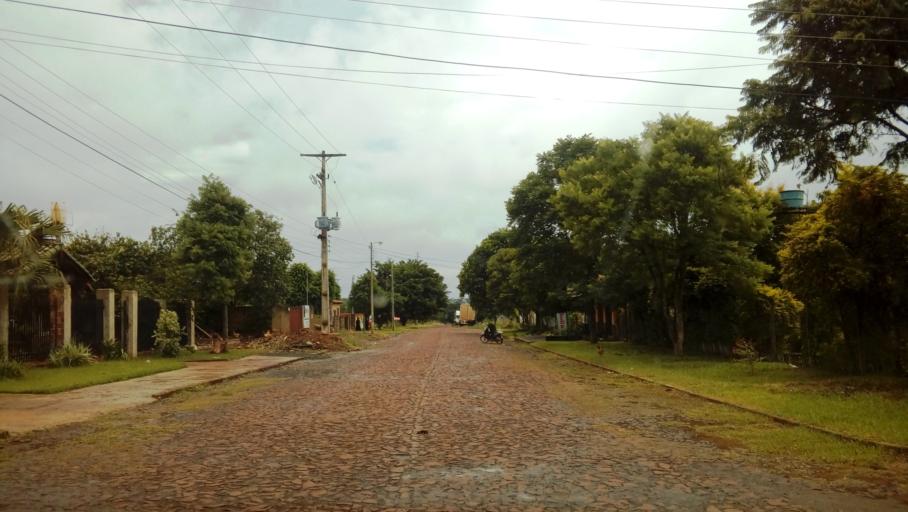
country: PY
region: Alto Parana
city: Ciudad del Este
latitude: -25.4267
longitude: -54.6427
